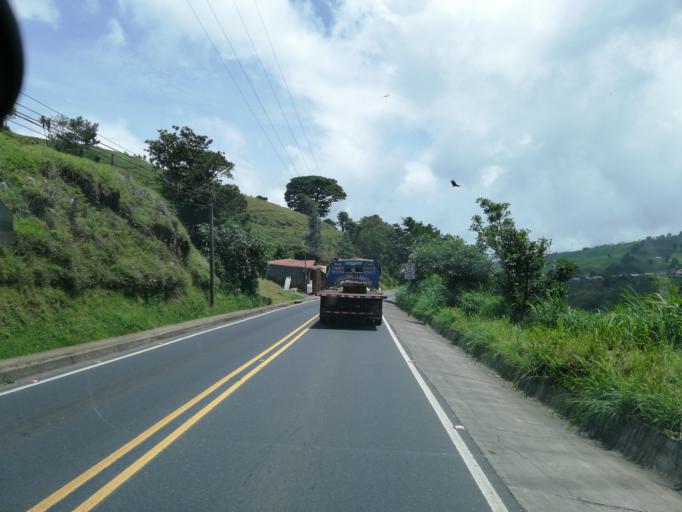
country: CR
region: Alajuela
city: Zarcero
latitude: 10.2197
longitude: -84.4039
